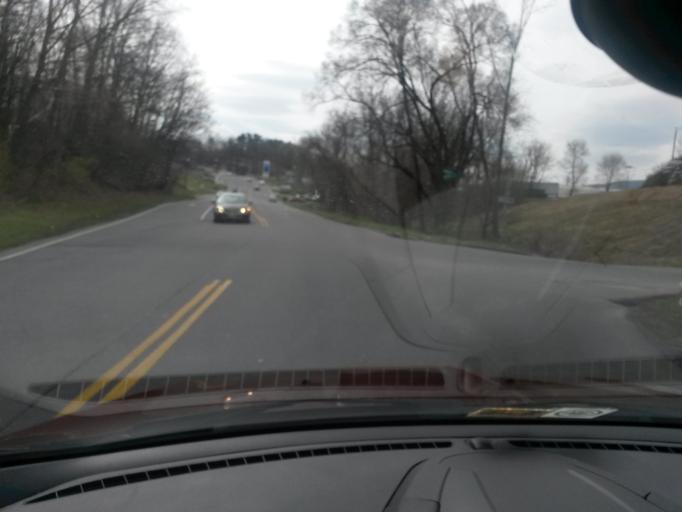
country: US
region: Virginia
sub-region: Roanoke County
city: Cave Spring
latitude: 37.2369
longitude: -80.0081
